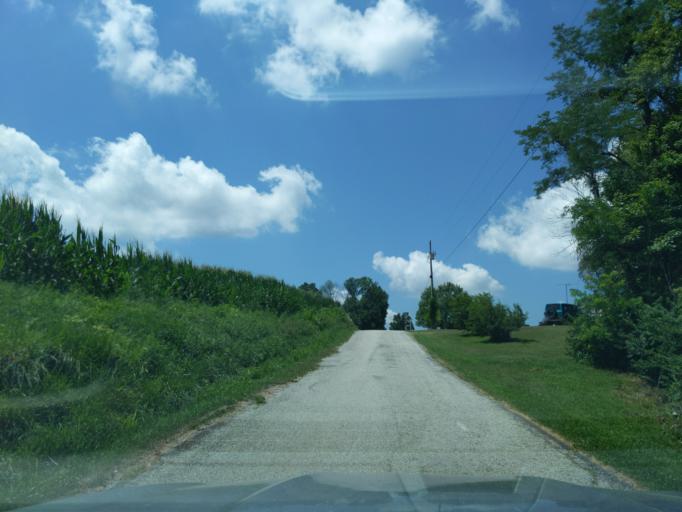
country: US
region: Indiana
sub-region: Ripley County
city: Osgood
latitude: 39.2201
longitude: -85.3918
